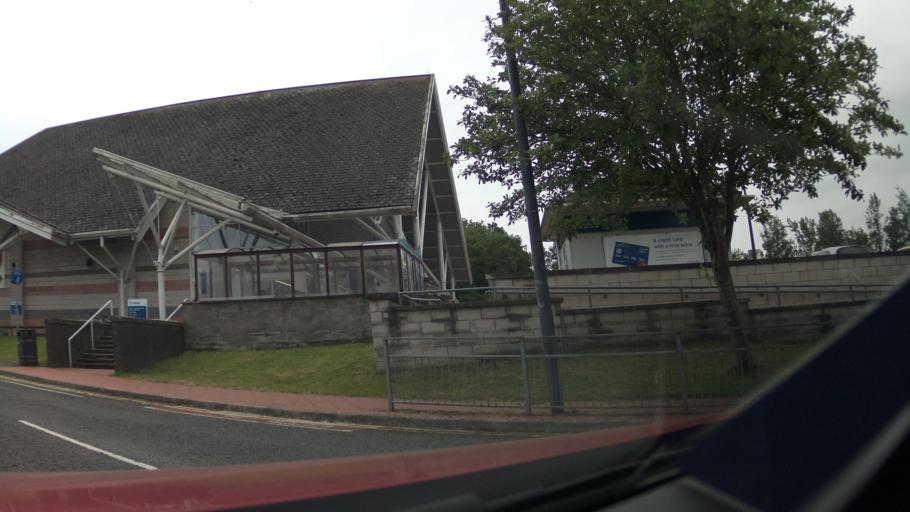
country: GB
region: Wales
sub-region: Vale of Glamorgan
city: Penarth
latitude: 51.4464
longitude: -3.1856
